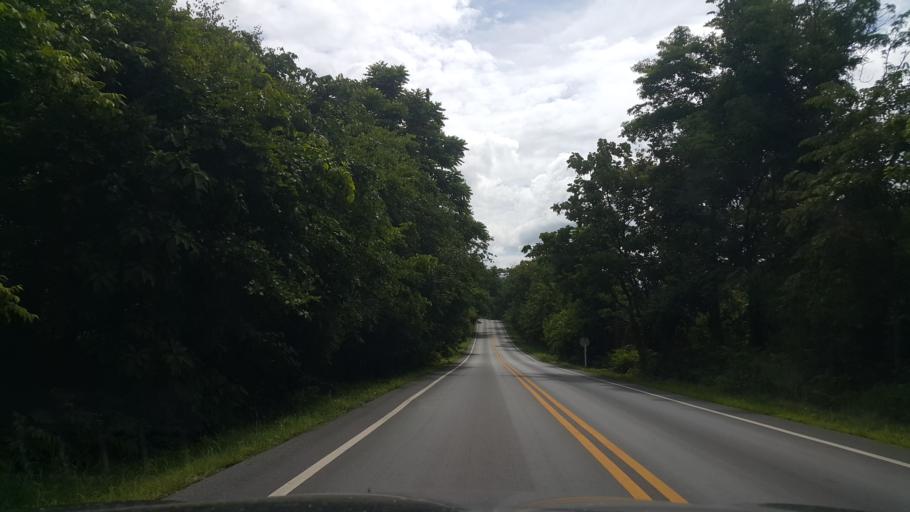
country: TH
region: Uttaradit
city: Thong Saen Khan
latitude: 17.3819
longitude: 100.2845
